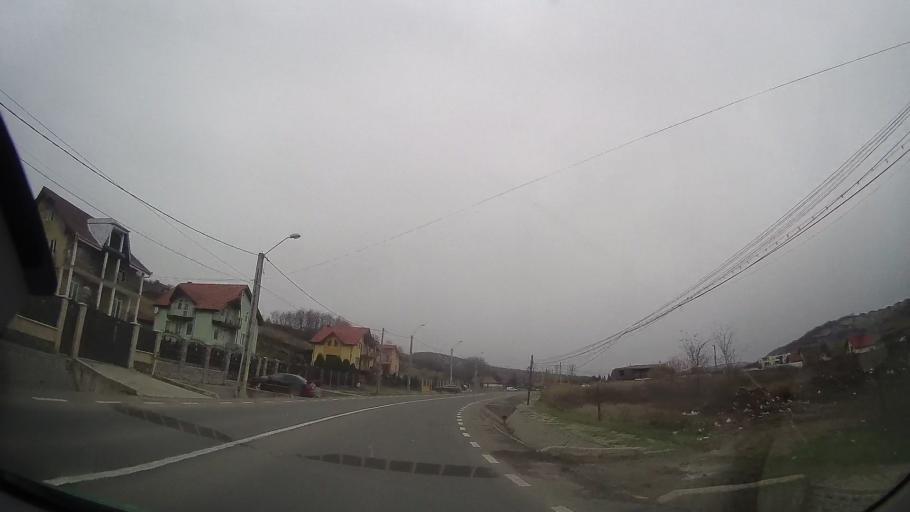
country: RO
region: Mures
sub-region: Comuna Ceausu de Campie
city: Ceausu de Campie
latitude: 46.6037
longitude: 24.5300
